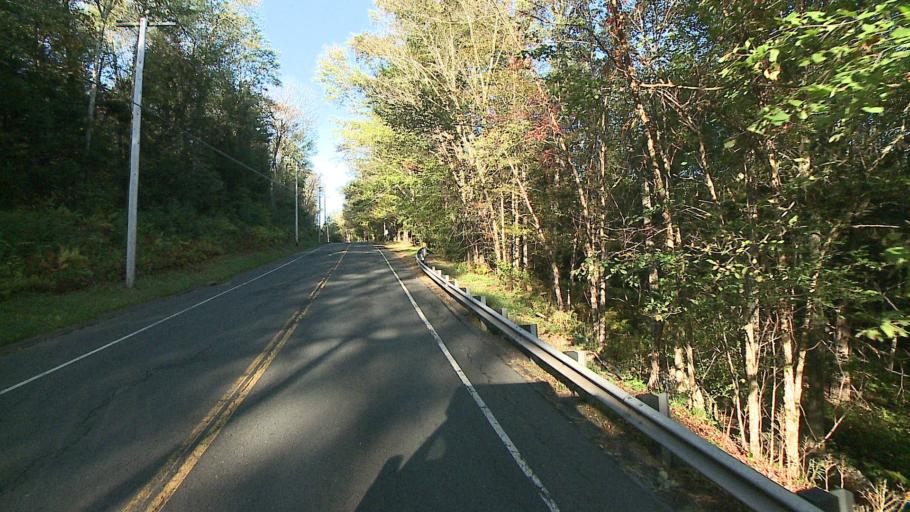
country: US
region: Connecticut
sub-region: Litchfield County
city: New Hartford Center
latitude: 41.8304
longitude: -72.9828
